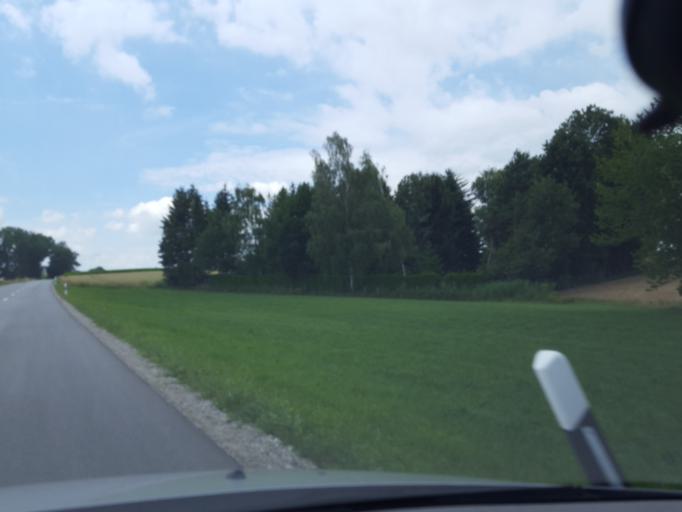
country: DE
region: Bavaria
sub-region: Lower Bavaria
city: Schalkham
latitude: 48.4464
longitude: 12.4079
